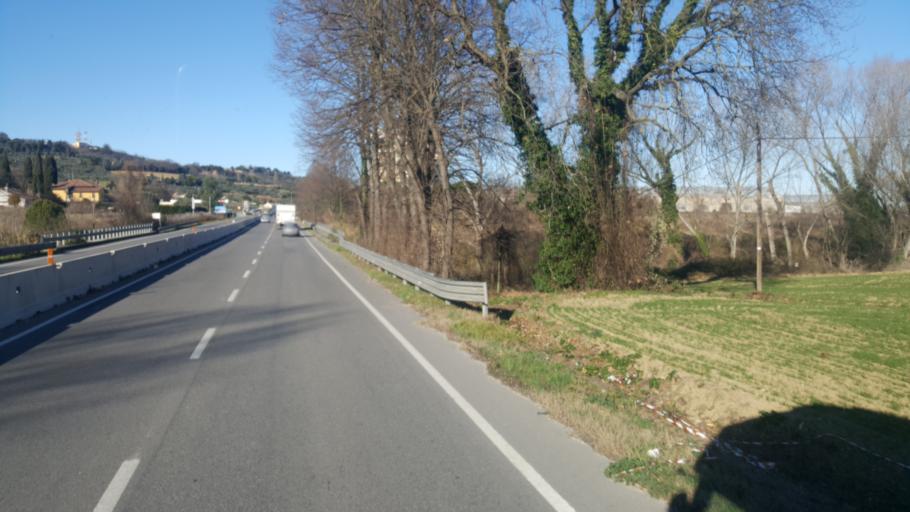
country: IT
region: Emilia-Romagna
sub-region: Provincia di Rimini
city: Cerasolo
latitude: 44.0153
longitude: 12.5467
